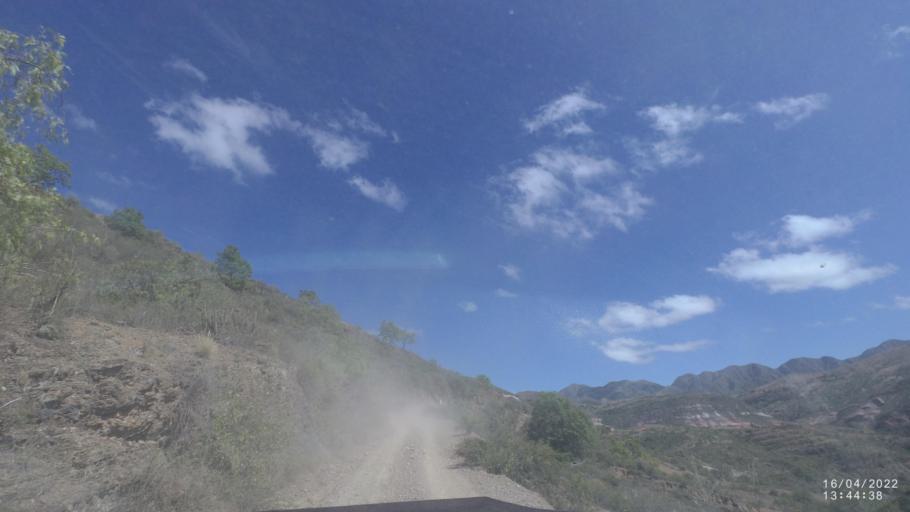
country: BO
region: Cochabamba
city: Mizque
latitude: -17.9994
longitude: -65.5921
